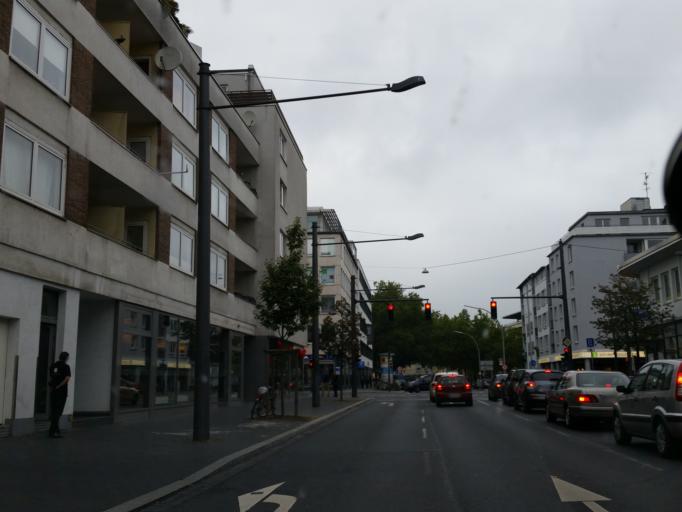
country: DE
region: Lower Saxony
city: Braunschweig
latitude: 52.2649
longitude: 10.5279
